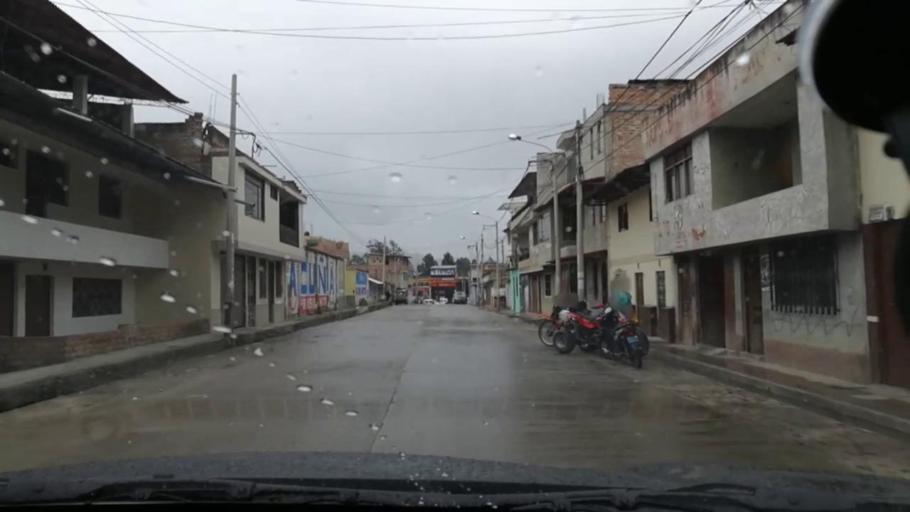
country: PE
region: Cajamarca
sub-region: Provincia de Cajamarca
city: Cajamarca
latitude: -7.1620
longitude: -78.5066
